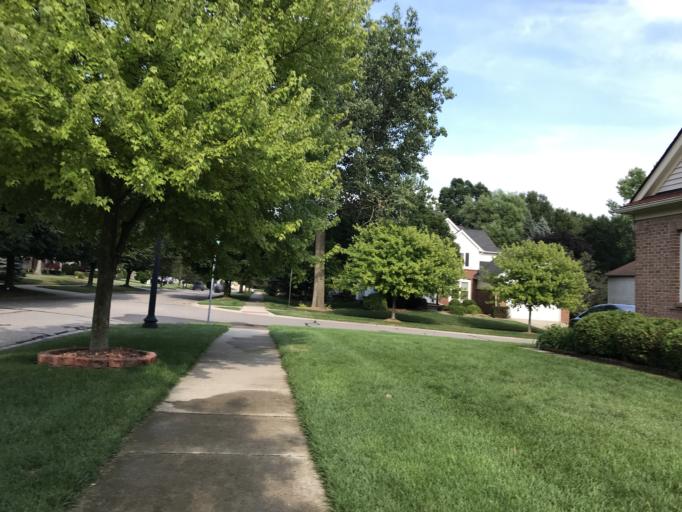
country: US
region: Michigan
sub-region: Oakland County
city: Franklin
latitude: 42.4974
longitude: -83.3351
